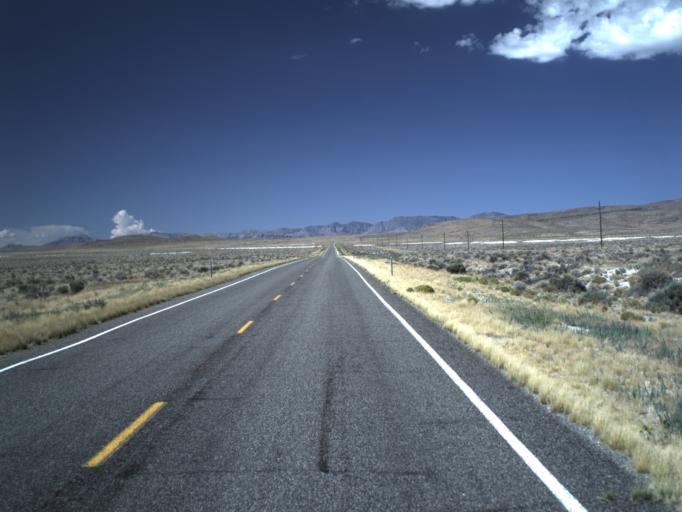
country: US
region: Utah
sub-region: Beaver County
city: Milford
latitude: 39.0675
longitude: -113.2290
